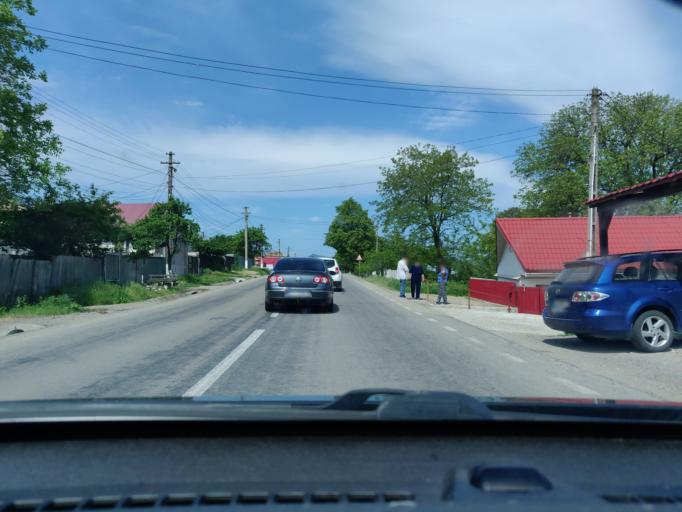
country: RO
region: Vrancea
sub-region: Comuna Vidra
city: Burca
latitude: 45.9118
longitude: 26.9486
